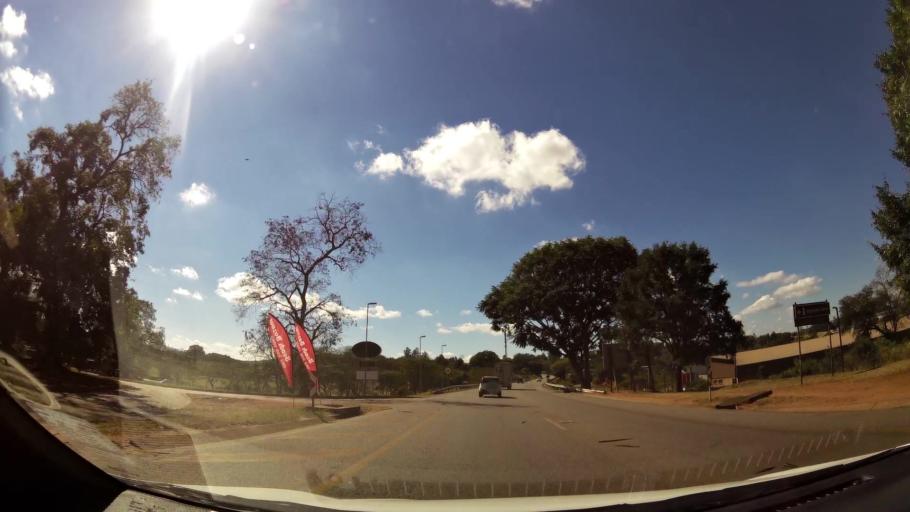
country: ZA
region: Limpopo
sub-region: Mopani District Municipality
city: Tzaneen
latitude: -23.8215
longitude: 30.1615
